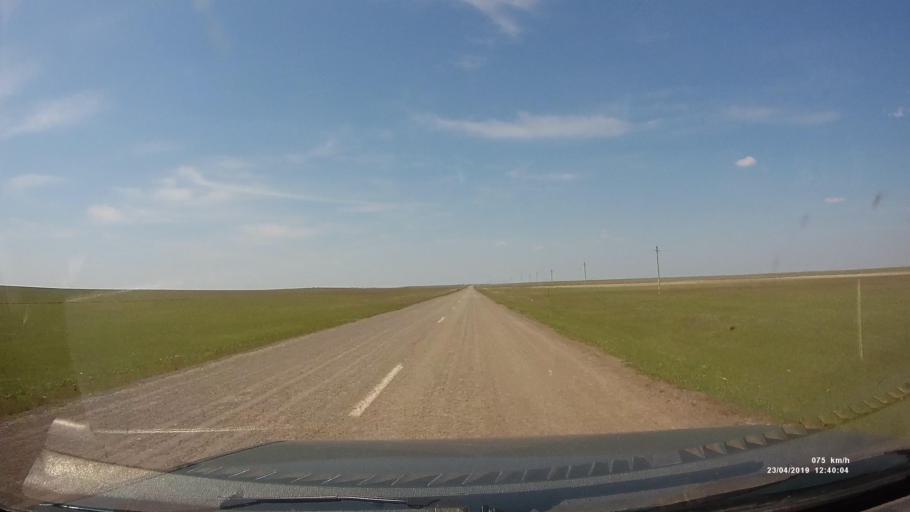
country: RU
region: Kalmykiya
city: Yashalta
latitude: 46.4378
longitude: 42.7018
